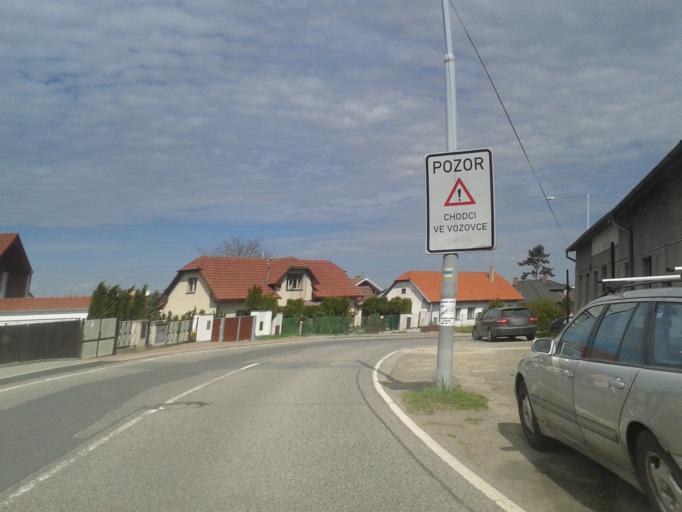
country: CZ
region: Central Bohemia
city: Vrane nad Vltavou
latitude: 49.9561
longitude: 14.3817
